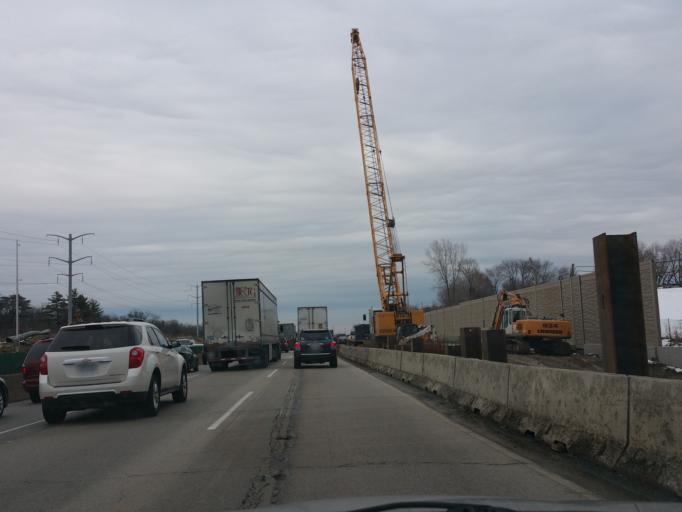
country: US
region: Illinois
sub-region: Cook County
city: South Barrington
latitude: 42.0665
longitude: -88.1121
